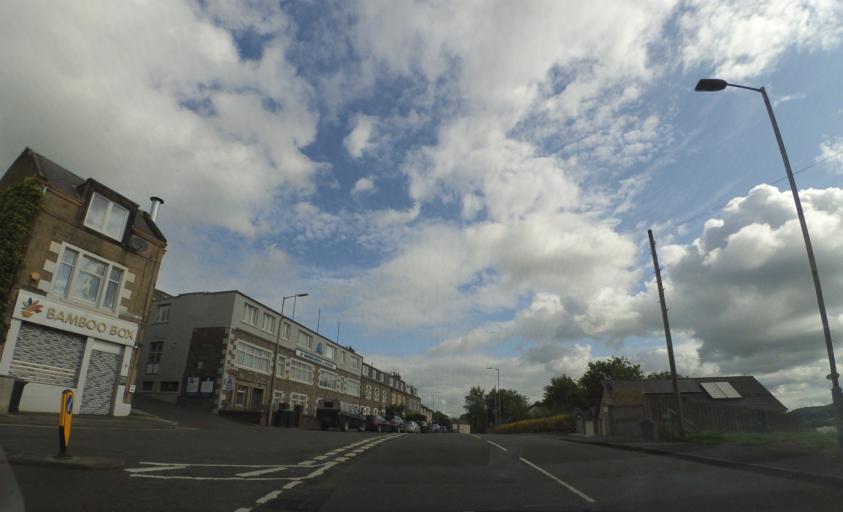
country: GB
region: Scotland
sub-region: The Scottish Borders
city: Hawick
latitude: 55.4256
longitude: -2.7907
